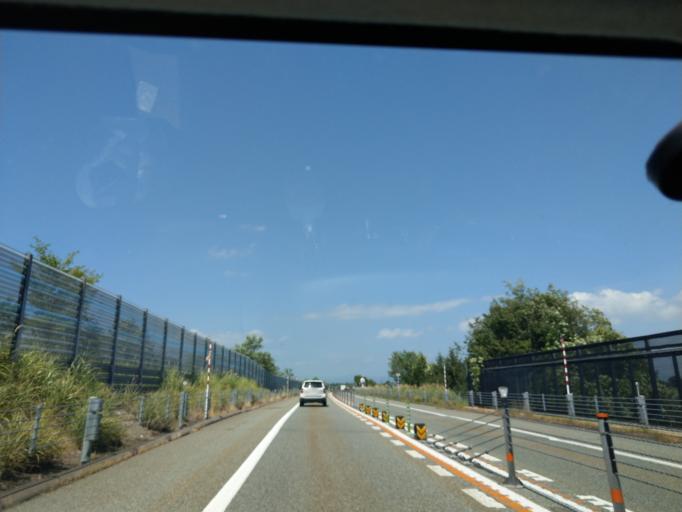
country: JP
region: Akita
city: Omagari
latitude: 39.3824
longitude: 140.4796
